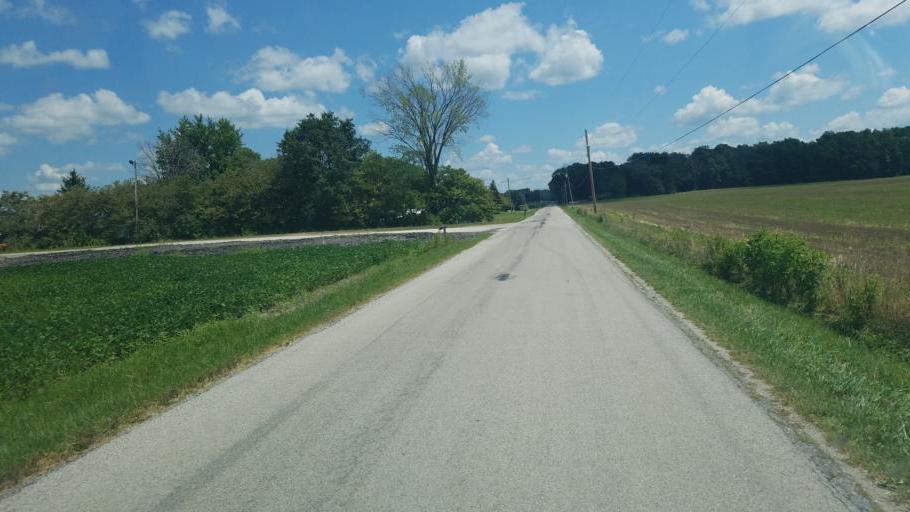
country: US
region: Ohio
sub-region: Marion County
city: Marion
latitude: 40.6591
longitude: -83.1267
